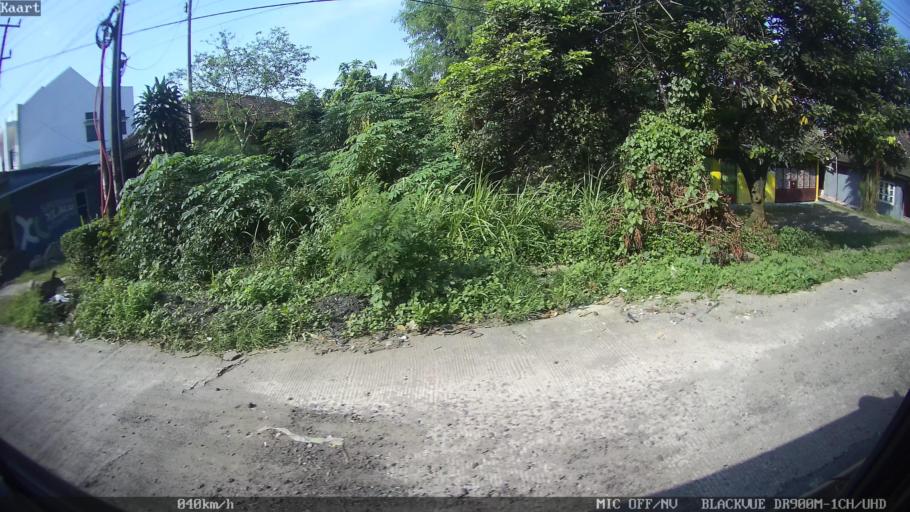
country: ID
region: Lampung
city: Natar
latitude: -5.3280
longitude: 105.2054
